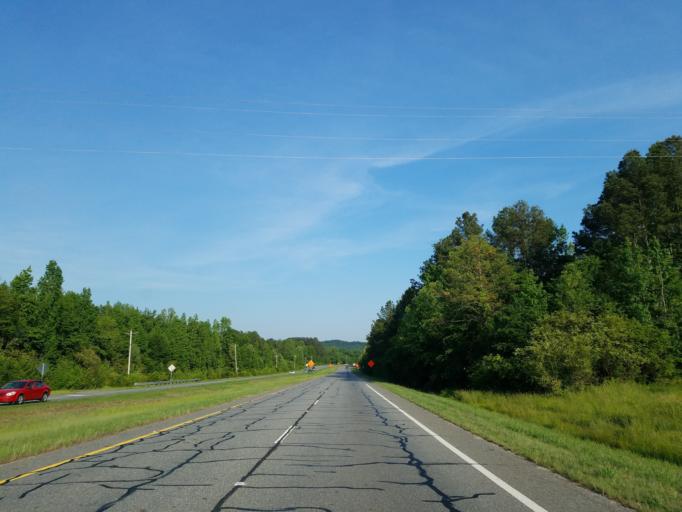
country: US
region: Georgia
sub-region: Chattooga County
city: Summerville
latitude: 34.4636
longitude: -85.2647
